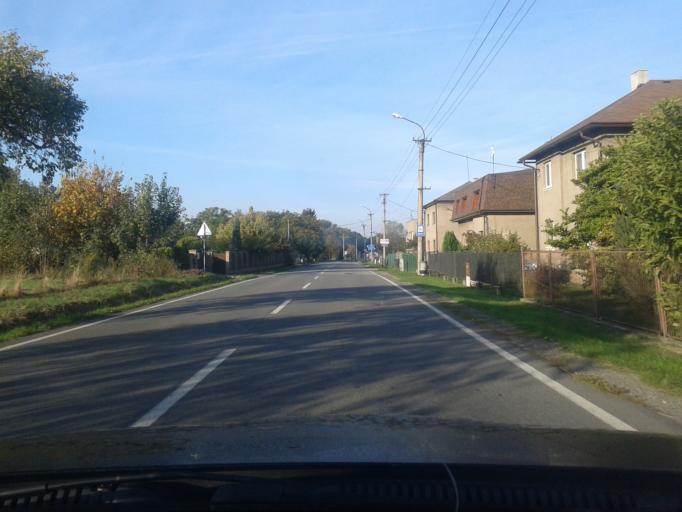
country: CZ
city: Rychvald
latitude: 49.8836
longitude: 18.3860
